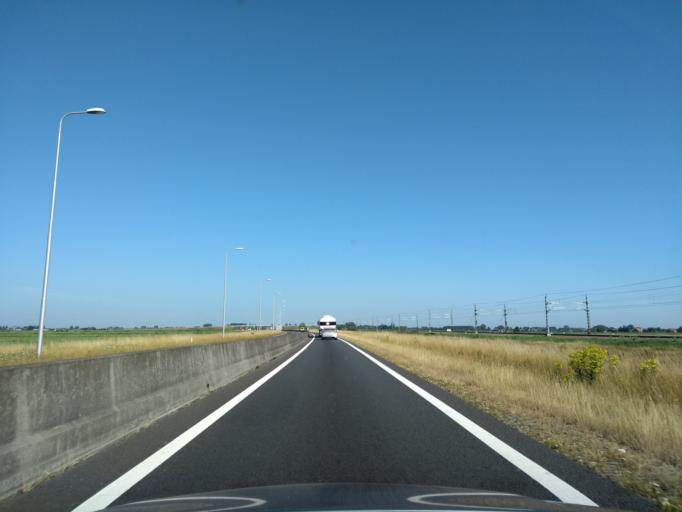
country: NL
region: Gelderland
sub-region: Gemeente Hattem
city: Hattem
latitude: 52.4965
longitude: 6.0096
